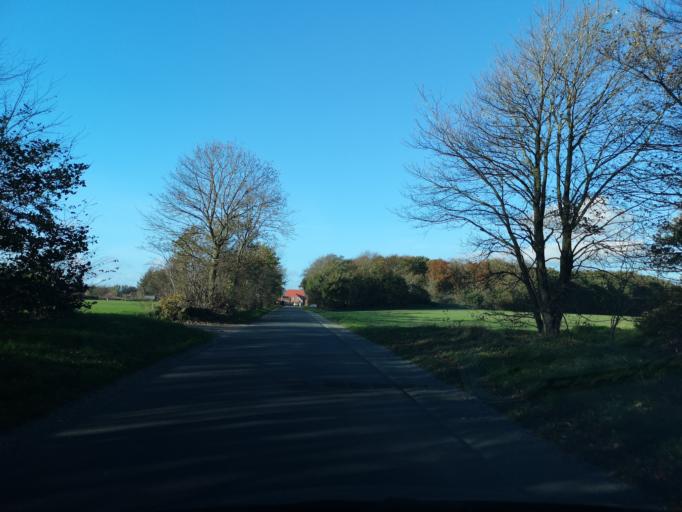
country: DK
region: Central Jutland
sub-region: Ringkobing-Skjern Kommune
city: Tarm
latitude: 55.8193
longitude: 8.4117
